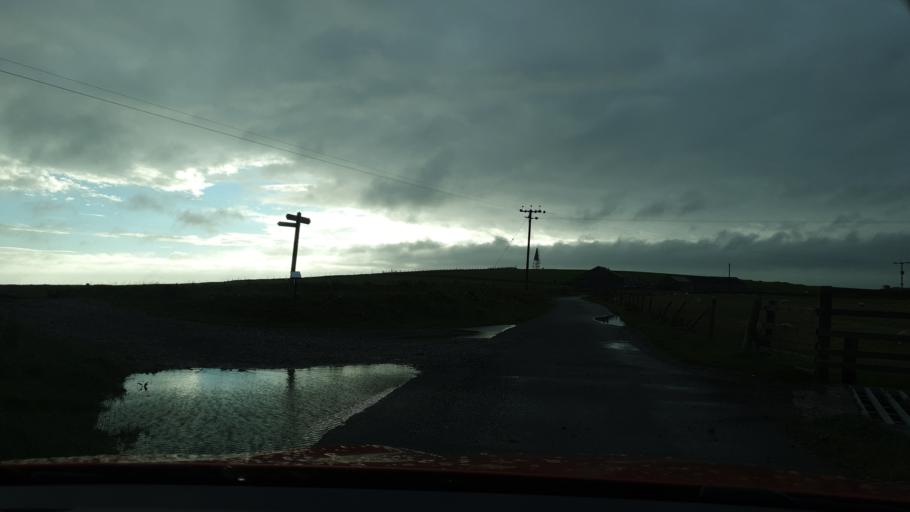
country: GB
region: England
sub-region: Cumbria
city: Barrow in Furness
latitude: 54.0555
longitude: -3.2128
